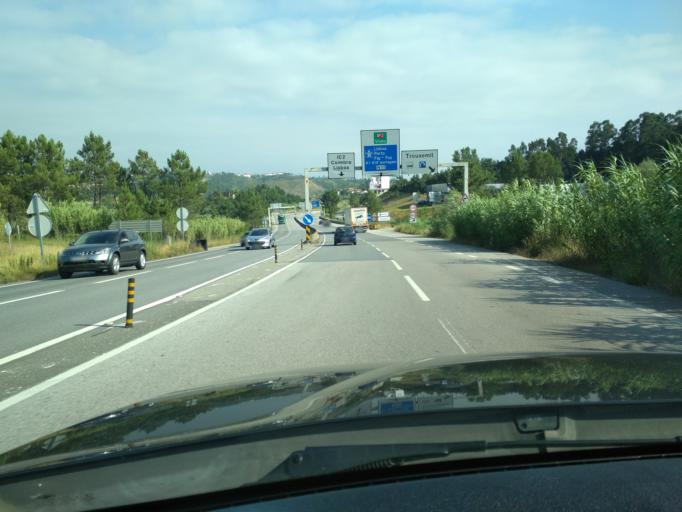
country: PT
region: Aveiro
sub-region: Mealhada
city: Pampilhosa do Botao
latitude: 40.2779
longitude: -8.4457
